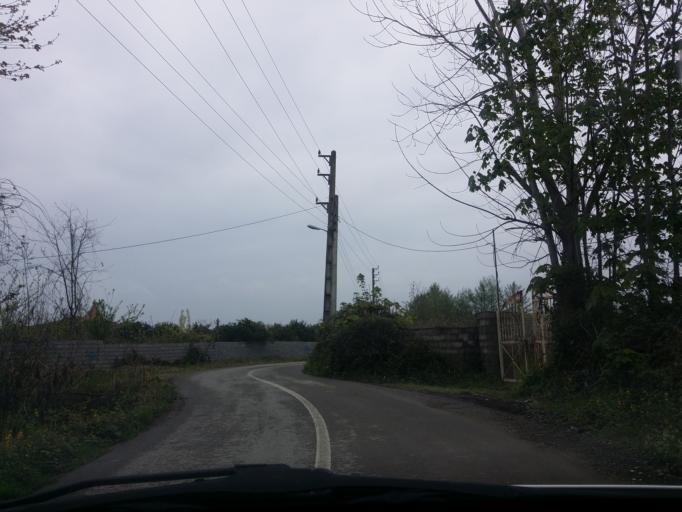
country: IR
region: Mazandaran
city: Chalus
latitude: 36.6775
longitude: 51.3786
